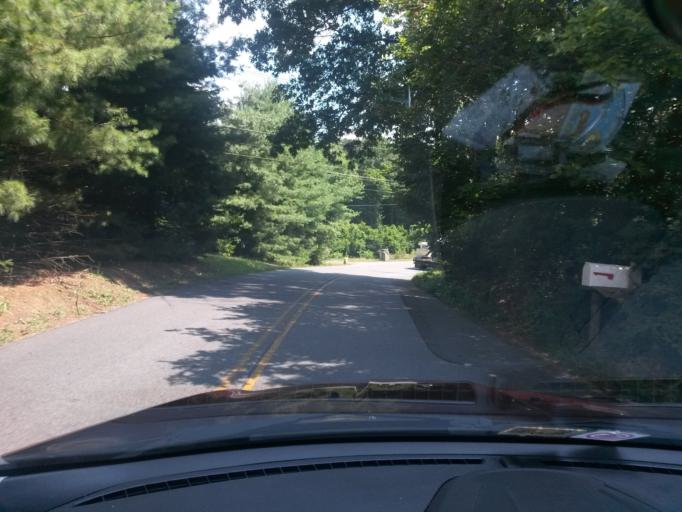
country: US
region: Virginia
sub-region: Giles County
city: Narrows
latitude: 37.3679
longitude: -80.8135
